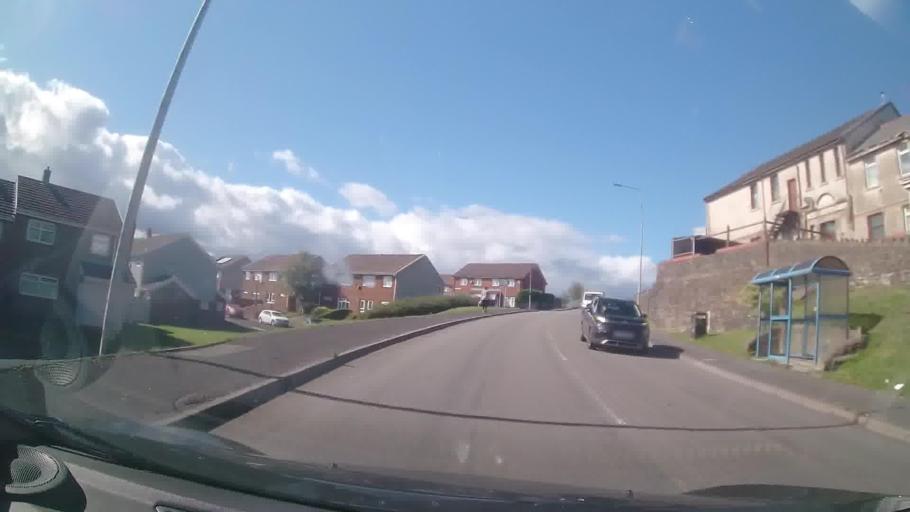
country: GB
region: Wales
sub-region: Merthyr Tydfil County Borough
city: Merthyr Tydfil
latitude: 51.7610
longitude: -3.3546
